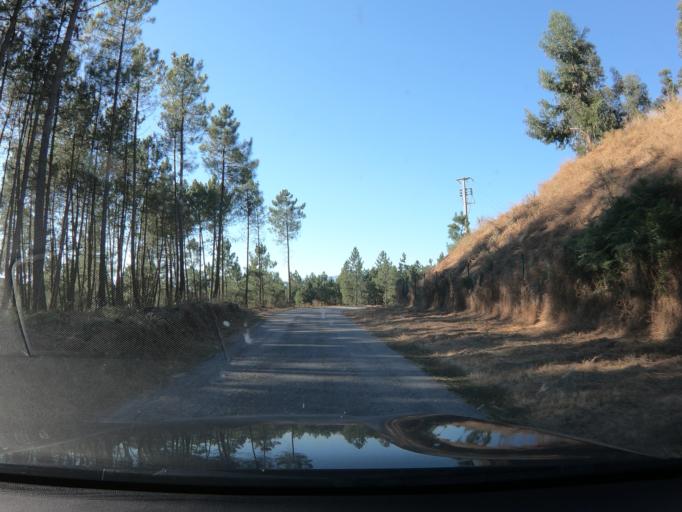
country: PT
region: Vila Real
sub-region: Sabrosa
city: Vilela
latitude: 41.2480
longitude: -7.6280
